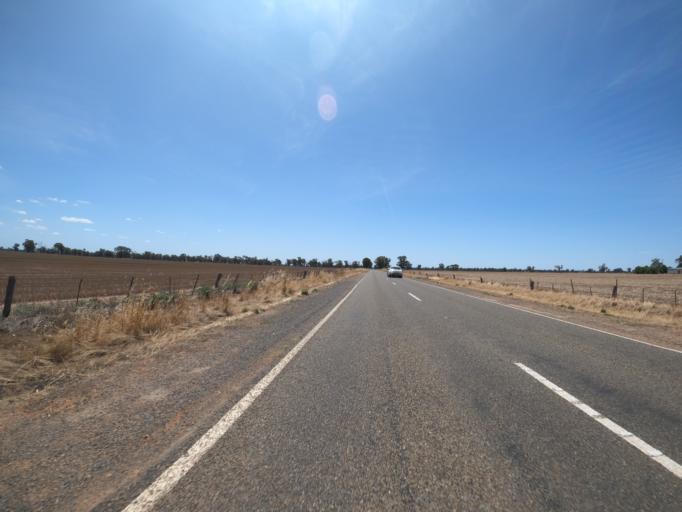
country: AU
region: Victoria
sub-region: Moira
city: Yarrawonga
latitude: -36.1775
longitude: 145.9672
